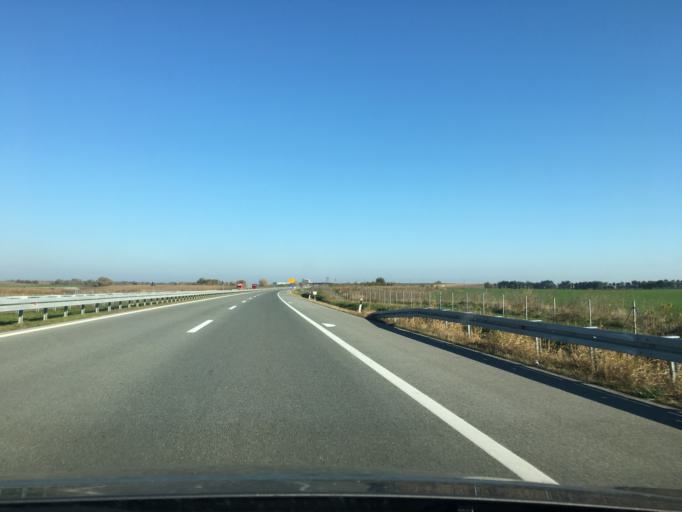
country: RS
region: Autonomna Pokrajina Vojvodina
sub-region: Severnobacki Okrug
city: Mali Igos
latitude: 45.6329
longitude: 19.7088
